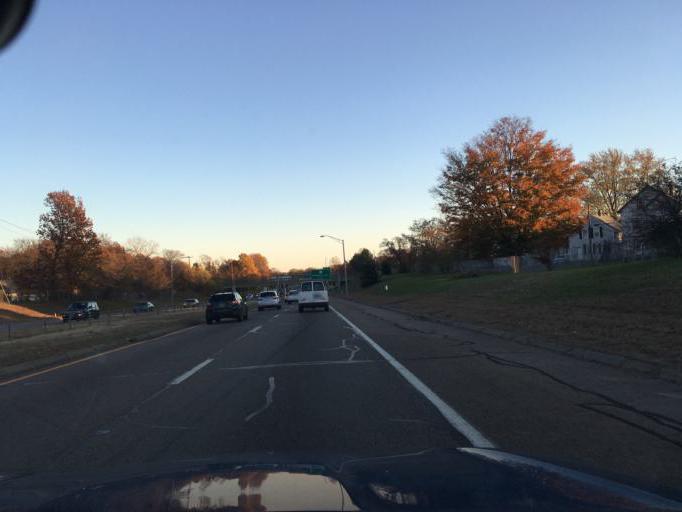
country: US
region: Rhode Island
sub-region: Providence County
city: Cranston
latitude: 41.7905
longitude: -71.4381
